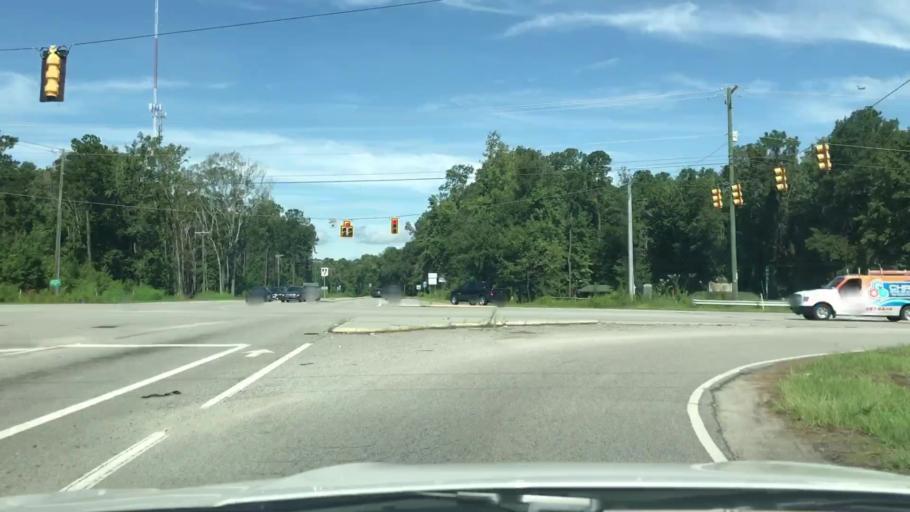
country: US
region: South Carolina
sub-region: Dorchester County
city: Centerville
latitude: 32.9481
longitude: -80.2050
